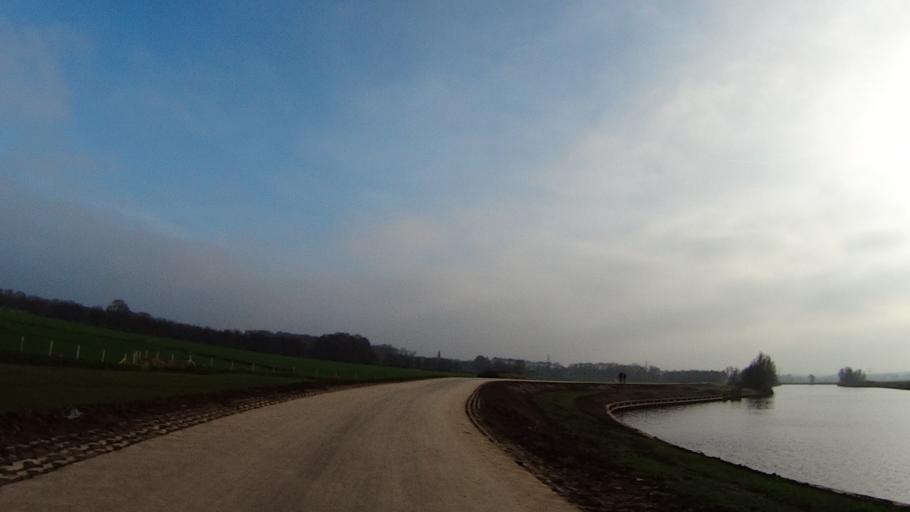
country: NL
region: Utrecht
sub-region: Gemeente Amersfoort
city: Hoogland
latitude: 52.1830
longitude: 5.3375
